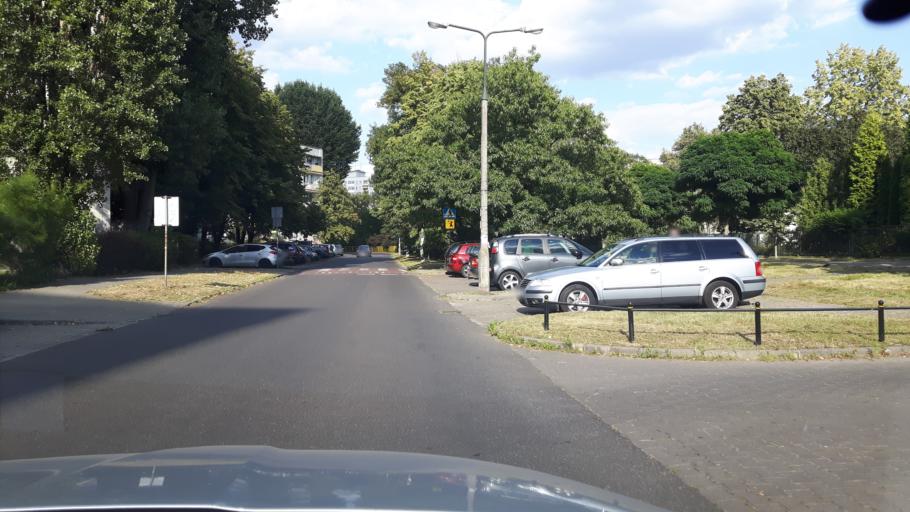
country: PL
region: Masovian Voivodeship
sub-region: Warszawa
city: Targowek
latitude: 52.2868
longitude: 21.0425
